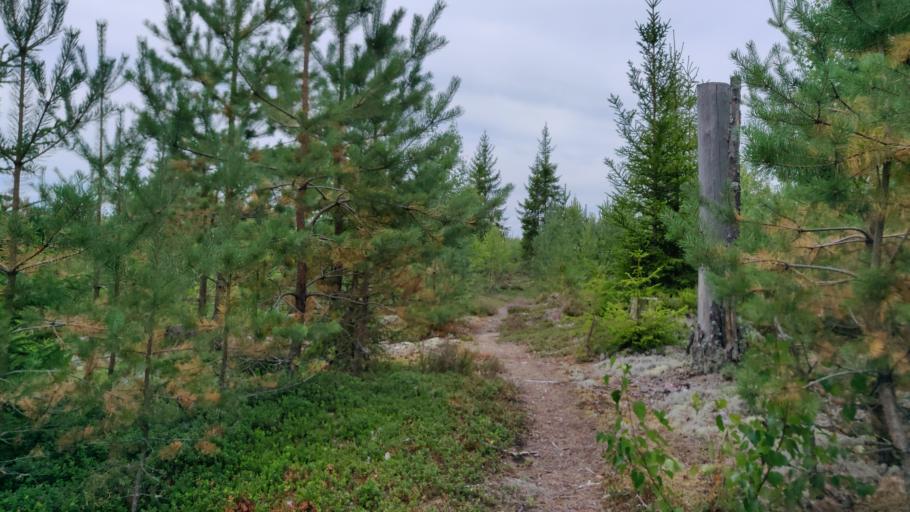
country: SE
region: Vaermland
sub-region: Hagfors Kommun
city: Hagfors
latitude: 60.0173
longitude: 13.5563
